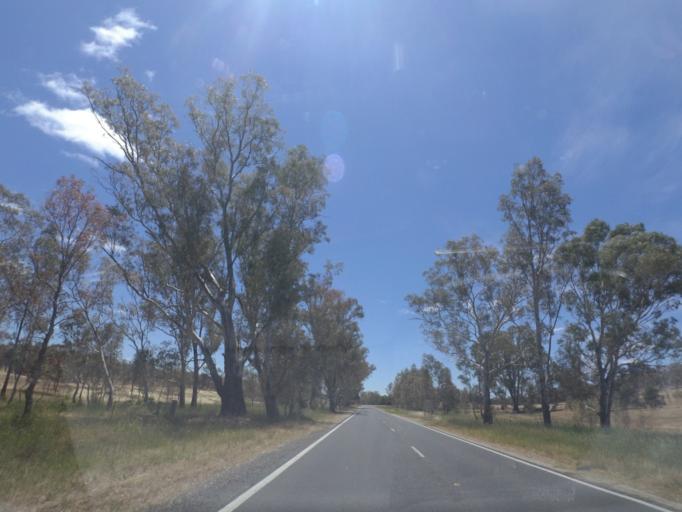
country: AU
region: Victoria
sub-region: Mount Alexander
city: Castlemaine
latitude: -37.1755
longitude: 144.1469
